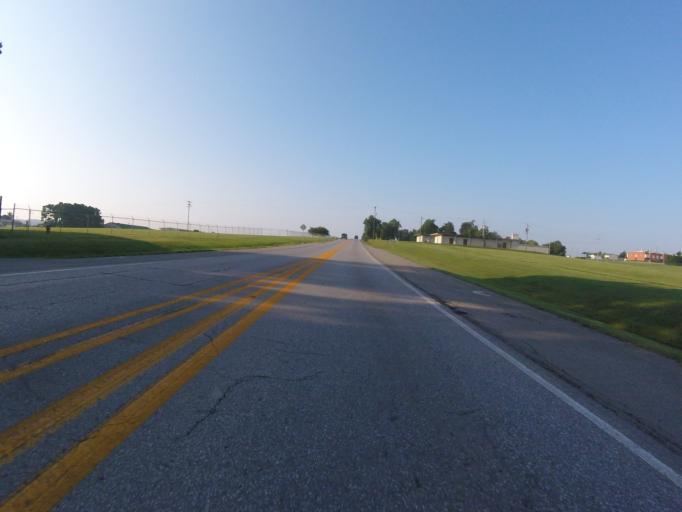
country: US
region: Arkansas
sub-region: Washington County
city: Johnson
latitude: 36.1020
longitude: -94.1775
